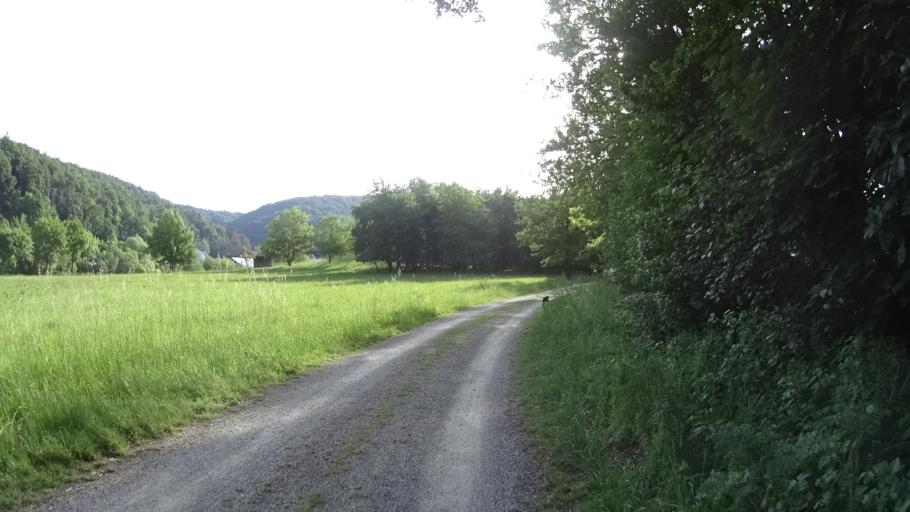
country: DE
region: Bavaria
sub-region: Lower Bavaria
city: Riedenburg
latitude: 48.9905
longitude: 11.6732
